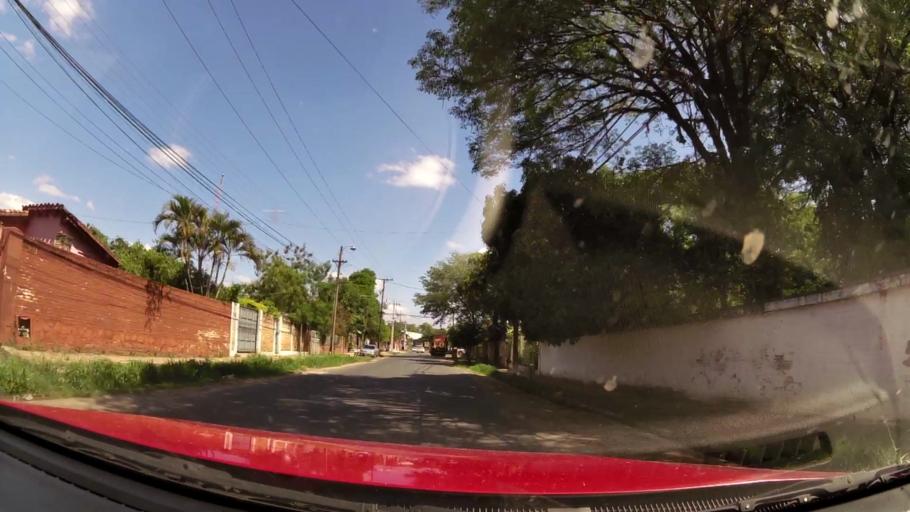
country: PY
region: Central
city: Colonia Mariano Roque Alonso
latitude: -25.2546
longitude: -57.5535
